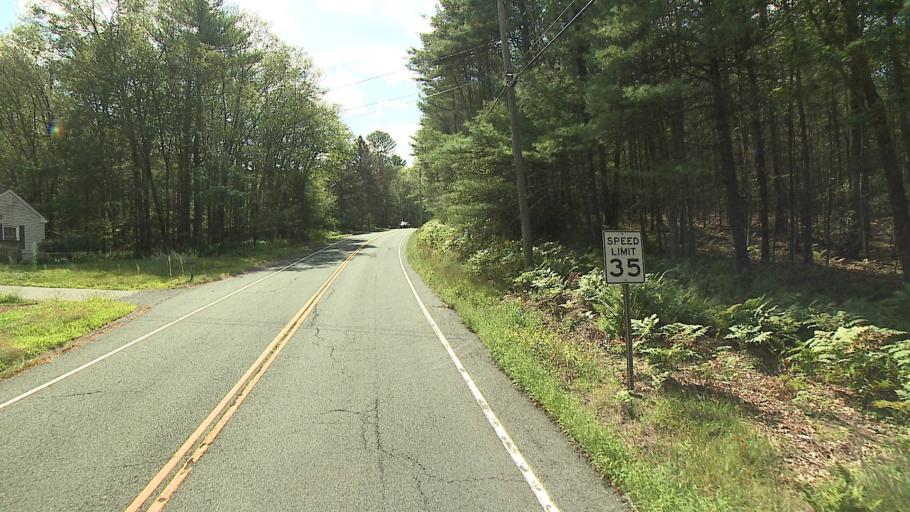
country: US
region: Connecticut
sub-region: Tolland County
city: Stafford Springs
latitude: 41.9447
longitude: -72.3337
